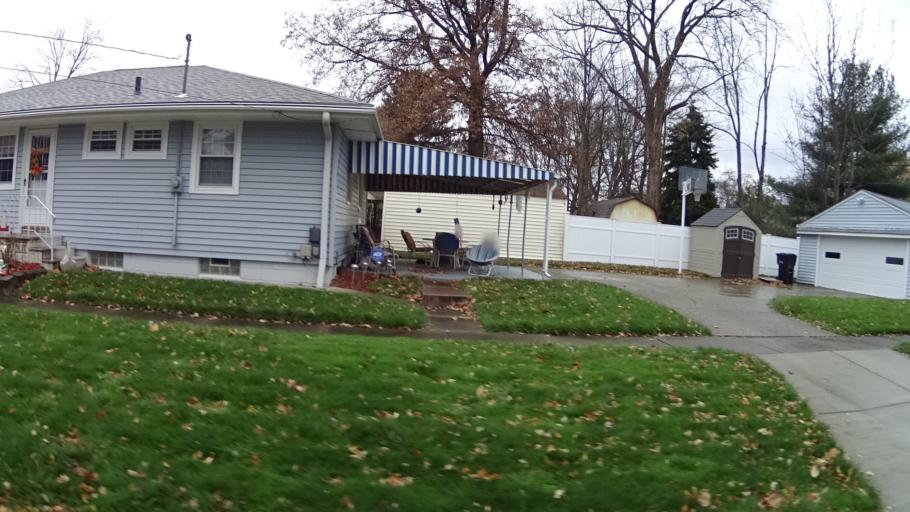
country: US
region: Ohio
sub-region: Lorain County
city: Elyria
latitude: 41.3843
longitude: -82.1314
